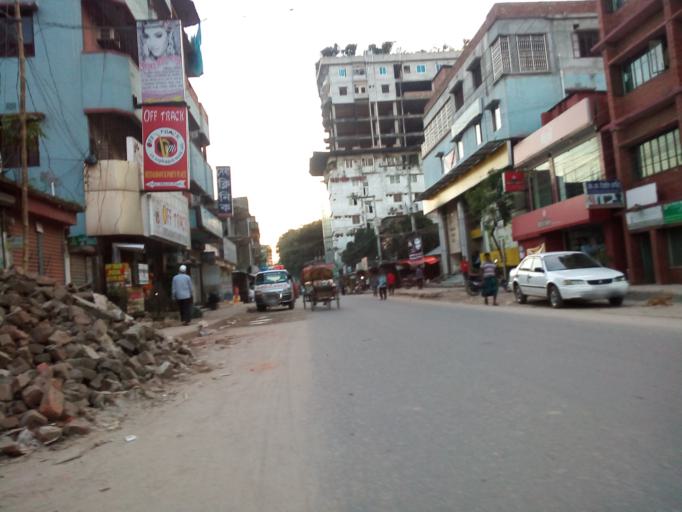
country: BD
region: Dhaka
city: Tungi
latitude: 23.8393
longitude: 90.2567
